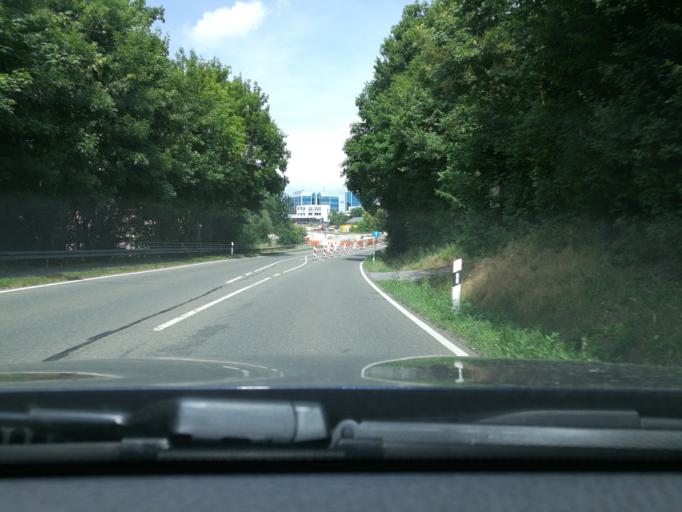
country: DE
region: Bavaria
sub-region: Regierungsbezirk Mittelfranken
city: Cadolzburg
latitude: 49.4721
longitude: 10.8615
